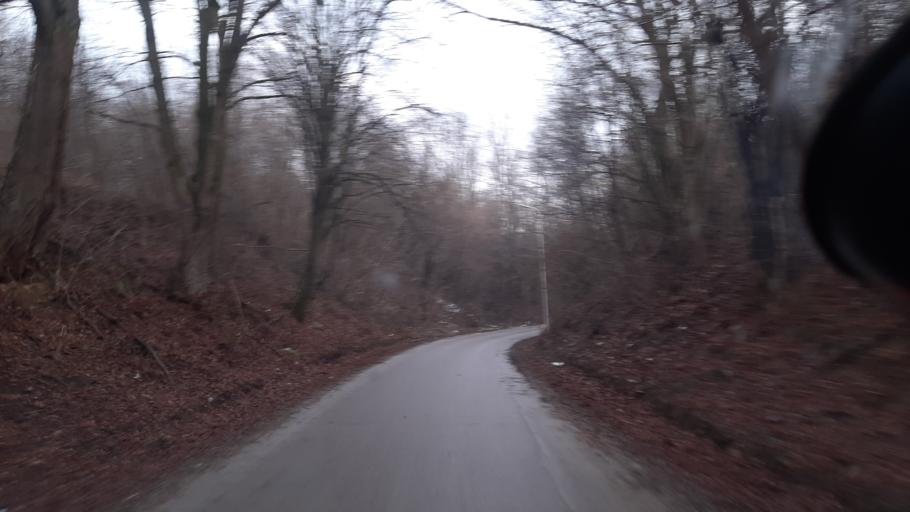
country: PL
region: Lublin Voivodeship
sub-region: Powiat lubelski
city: Lublin
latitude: 51.3159
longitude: 22.5783
